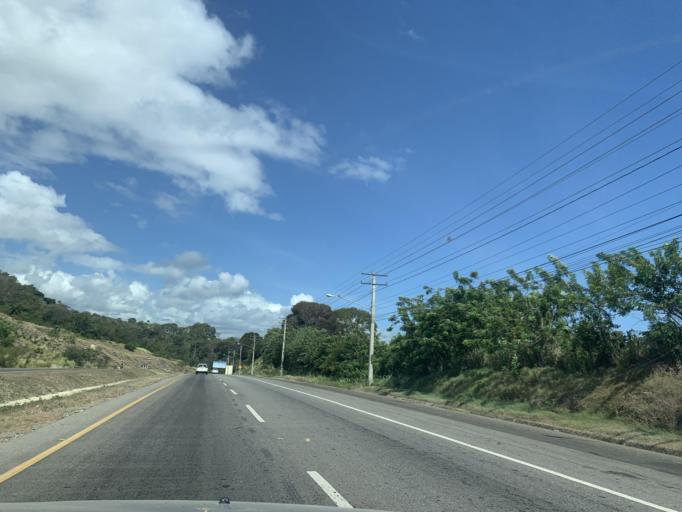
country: DO
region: Puerto Plata
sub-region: Puerto Plata
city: Puerto Plata
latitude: 19.8275
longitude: -70.7547
